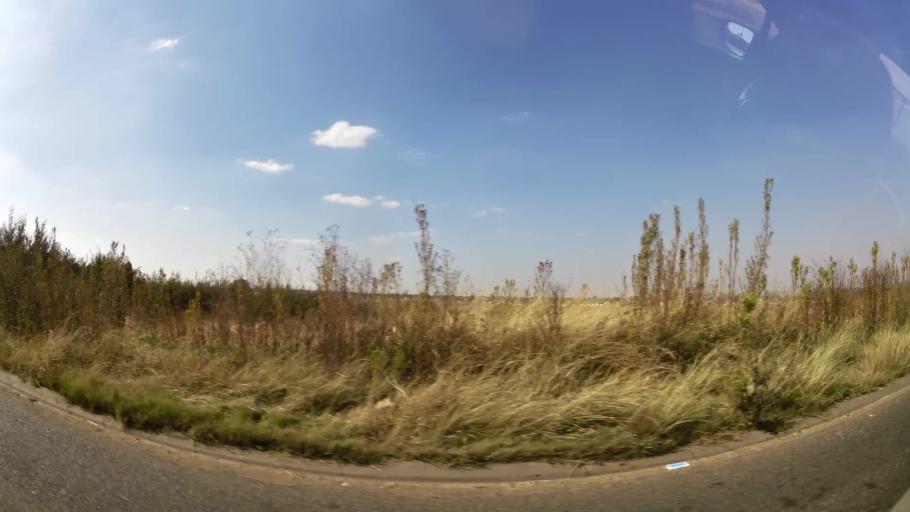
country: ZA
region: Gauteng
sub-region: City of Johannesburg Metropolitan Municipality
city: Roodepoort
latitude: -26.1588
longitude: 27.8048
